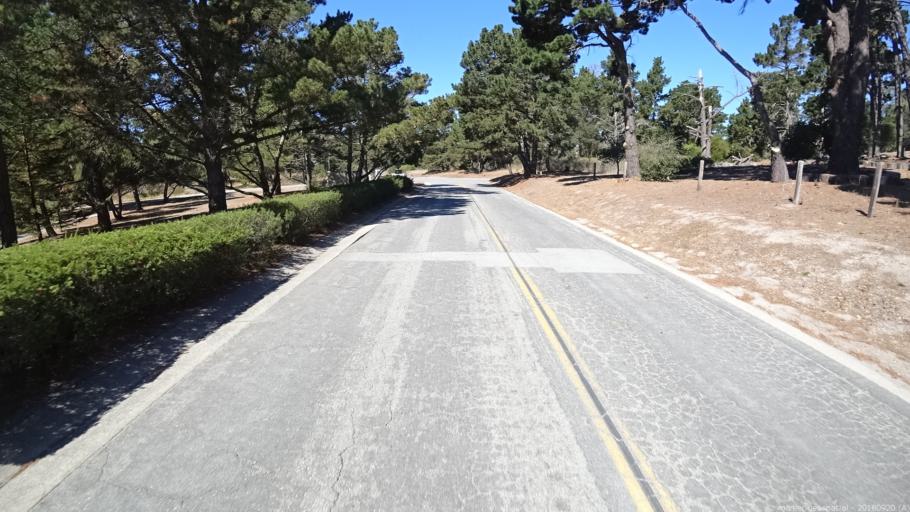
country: US
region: California
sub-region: Monterey County
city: Carmel-by-the-Sea
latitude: 36.5680
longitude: -121.9104
